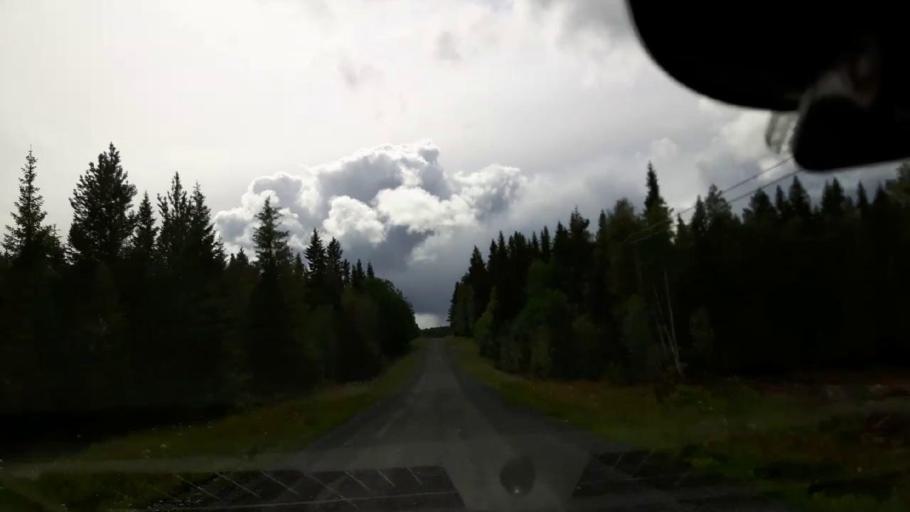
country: SE
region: Jaemtland
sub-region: Krokoms Kommun
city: Valla
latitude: 63.3614
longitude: 13.8615
